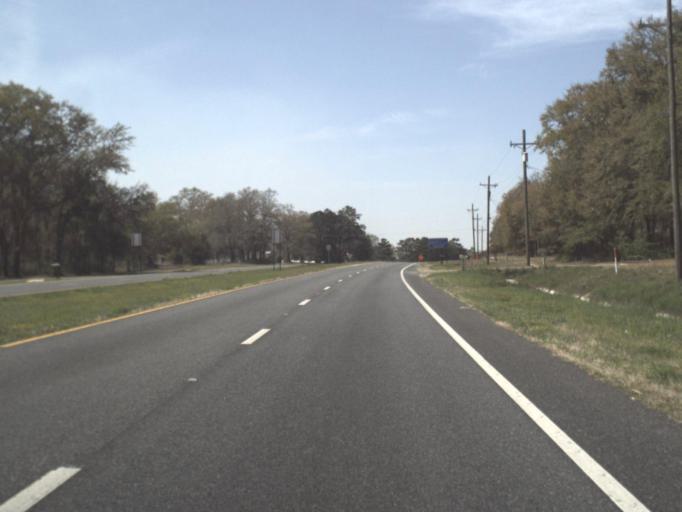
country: US
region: Florida
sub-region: Gadsden County
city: Quincy
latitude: 30.5560
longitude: -84.5297
